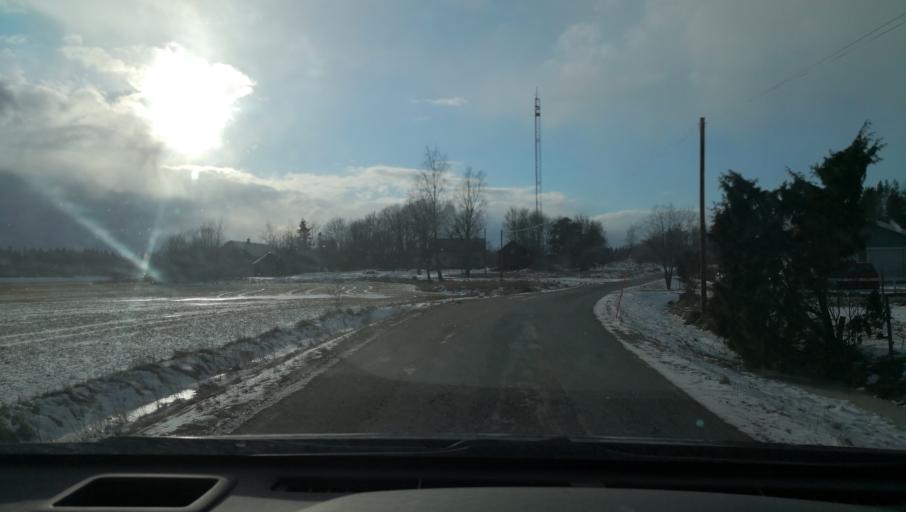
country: SE
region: Uppsala
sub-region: Enkopings Kommun
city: Irsta
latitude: 59.7084
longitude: 16.9034
